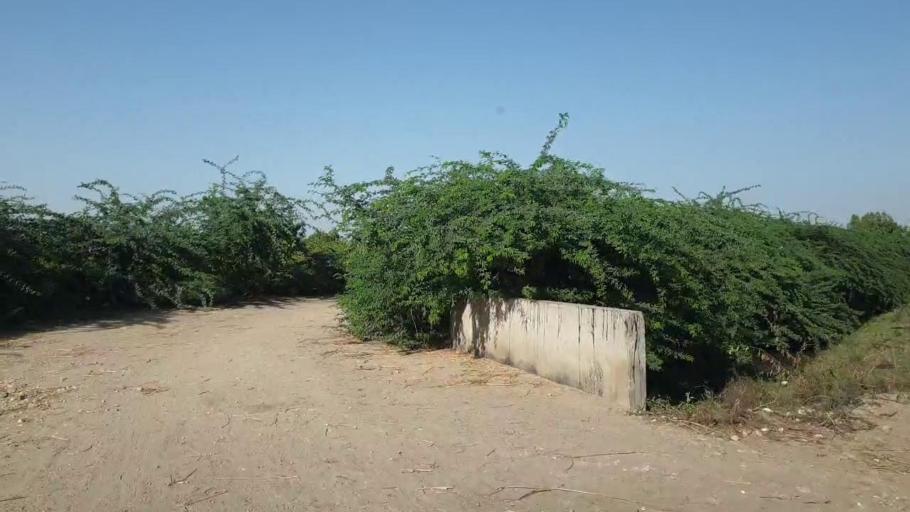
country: PK
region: Sindh
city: Badin
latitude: 24.6095
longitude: 68.9288
